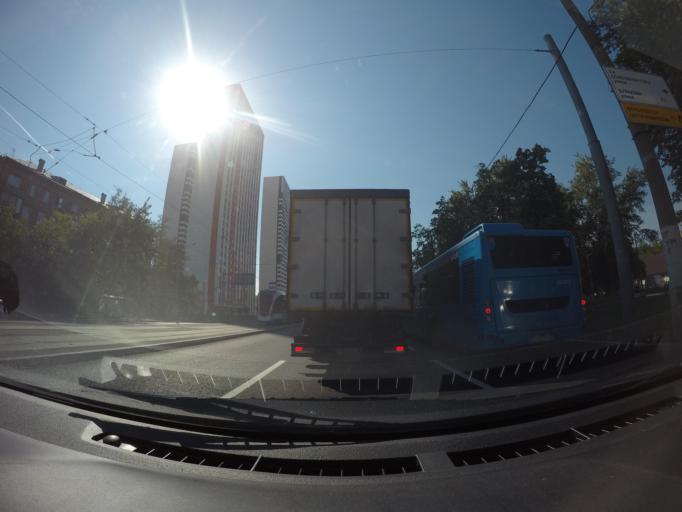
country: RU
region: Moscow
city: Lefortovo
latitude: 55.7613
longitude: 37.7360
